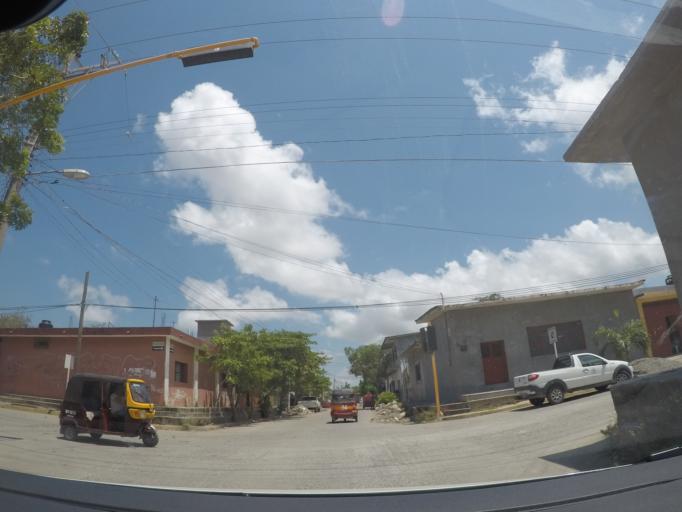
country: MX
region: Oaxaca
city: Juchitan de Zaragoza
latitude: 16.4341
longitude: -95.0159
